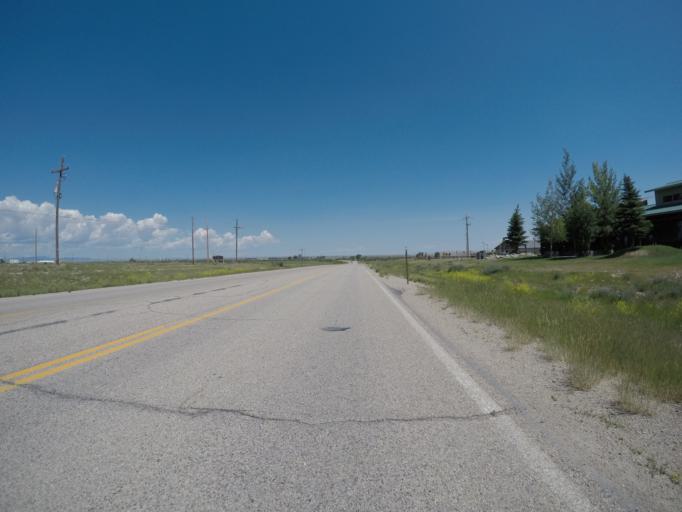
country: US
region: Wyoming
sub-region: Sublette County
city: Marbleton
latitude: 42.5130
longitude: -110.1049
